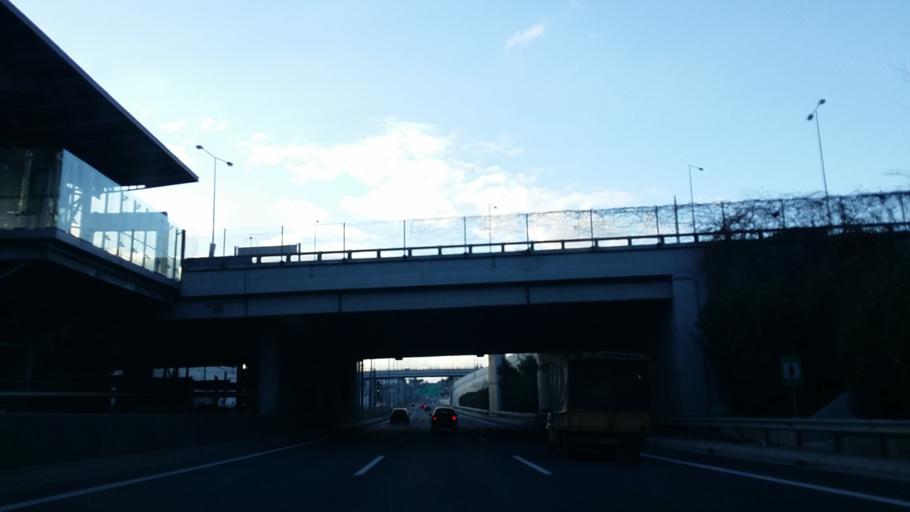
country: GR
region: Attica
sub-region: Nomarchia Athinas
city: Marousi
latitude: 38.0421
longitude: 23.8043
